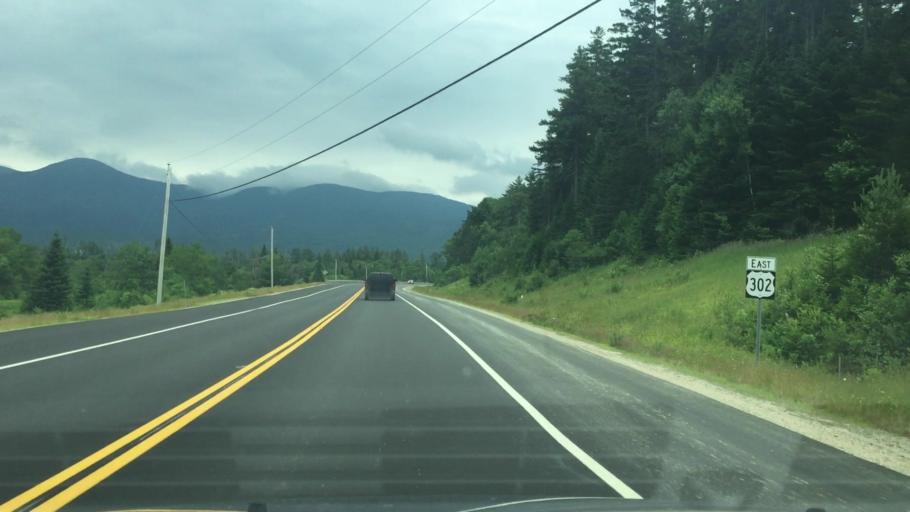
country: US
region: New Hampshire
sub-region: Coos County
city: Jefferson
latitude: 44.2533
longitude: -71.4480
